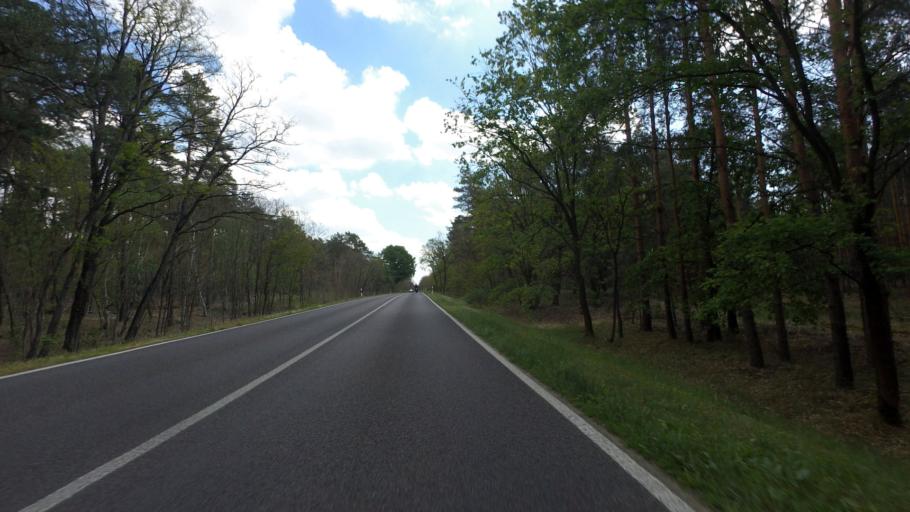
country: DE
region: Brandenburg
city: Neu Zauche
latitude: 51.9456
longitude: 14.0095
